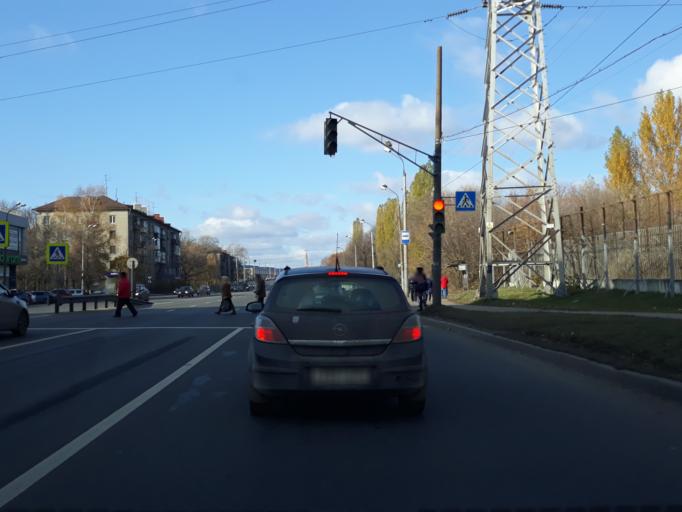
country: RU
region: Nizjnij Novgorod
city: Nizhniy Novgorod
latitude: 56.2650
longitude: 43.9204
